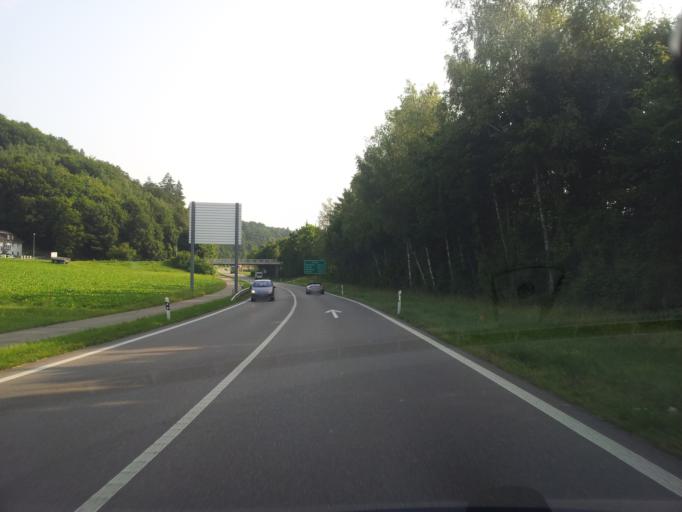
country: CH
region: Schaffhausen
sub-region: Bezirk Reiat
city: Stetten
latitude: 47.7205
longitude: 8.6679
